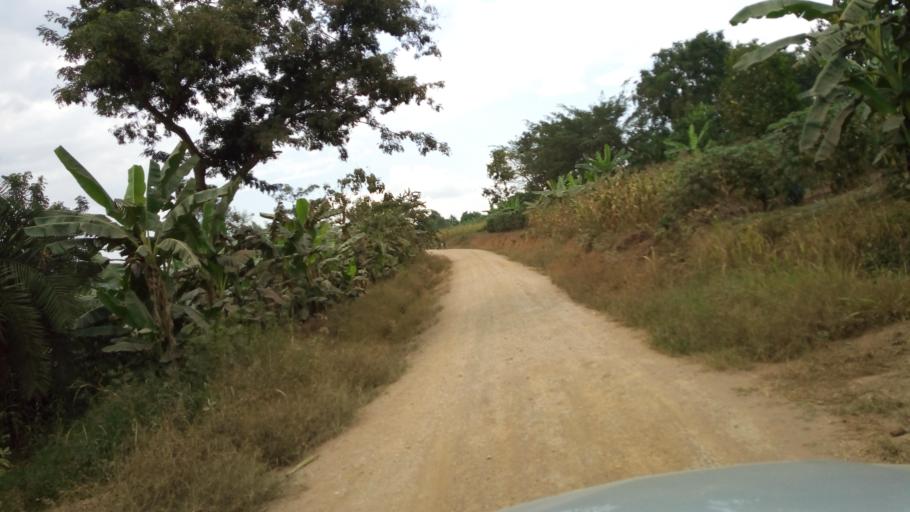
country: UG
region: Central Region
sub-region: Kiboga District
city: Kiboga
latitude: 0.7328
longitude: 31.7302
